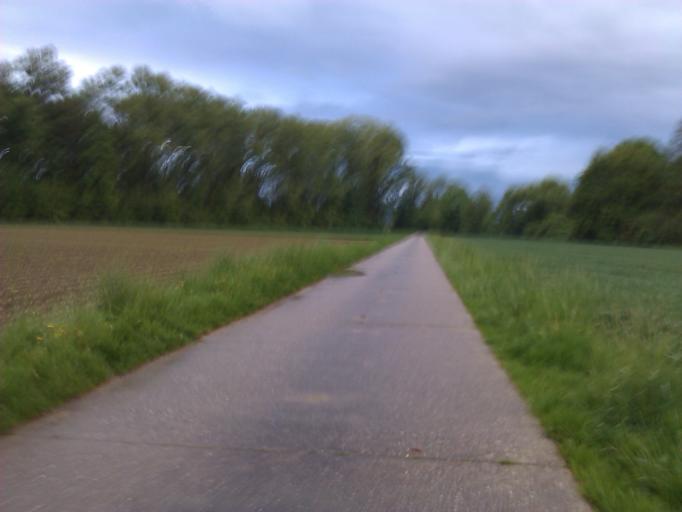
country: DE
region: Baden-Wuerttemberg
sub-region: Karlsruhe Region
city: Lichtenau
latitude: 48.6998
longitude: 7.9688
